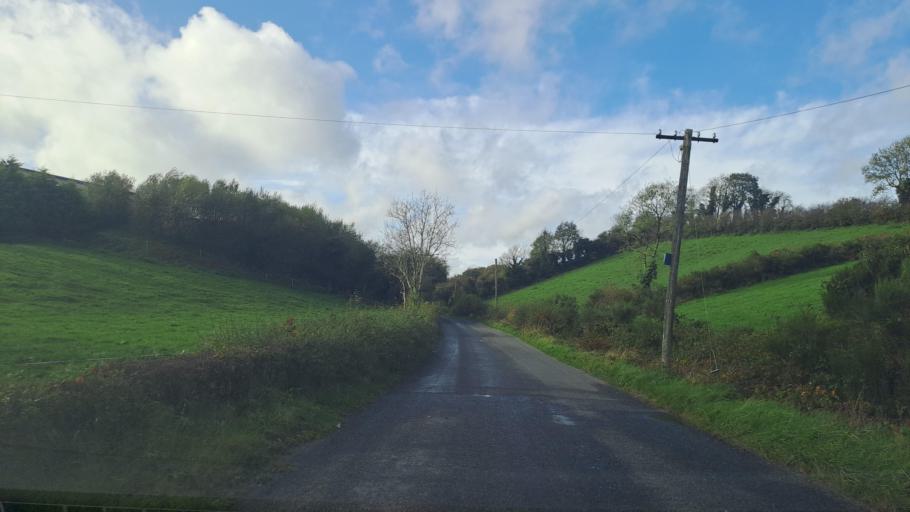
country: IE
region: Ulster
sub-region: An Cabhan
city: Cootehill
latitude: 54.0287
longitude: -7.0299
